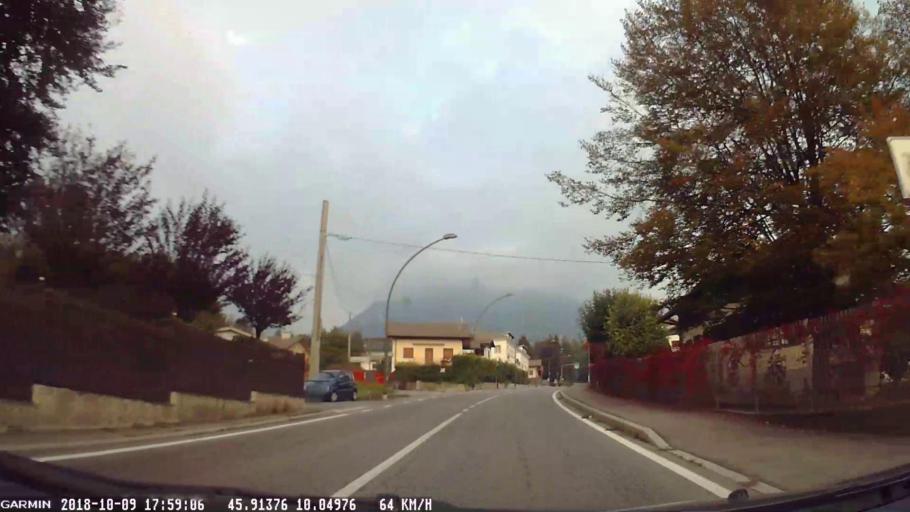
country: IT
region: Lombardy
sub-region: Provincia di Bergamo
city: Castione della Presolana
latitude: 45.9111
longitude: 10.0413
